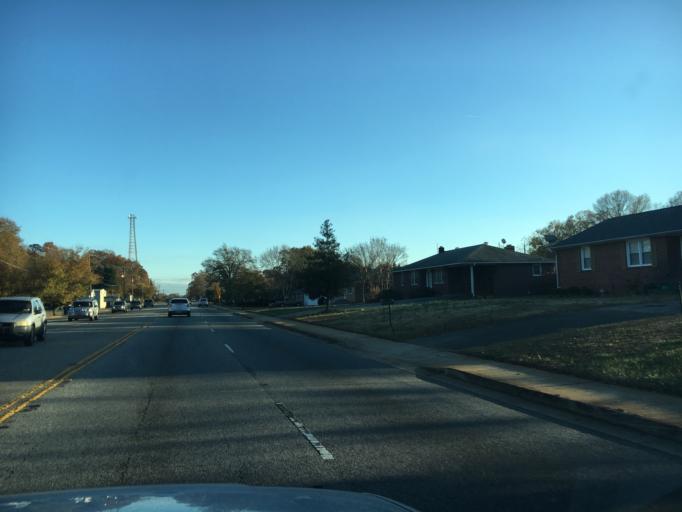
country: US
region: South Carolina
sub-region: Spartanburg County
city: Lyman
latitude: 34.9276
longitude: -82.1213
